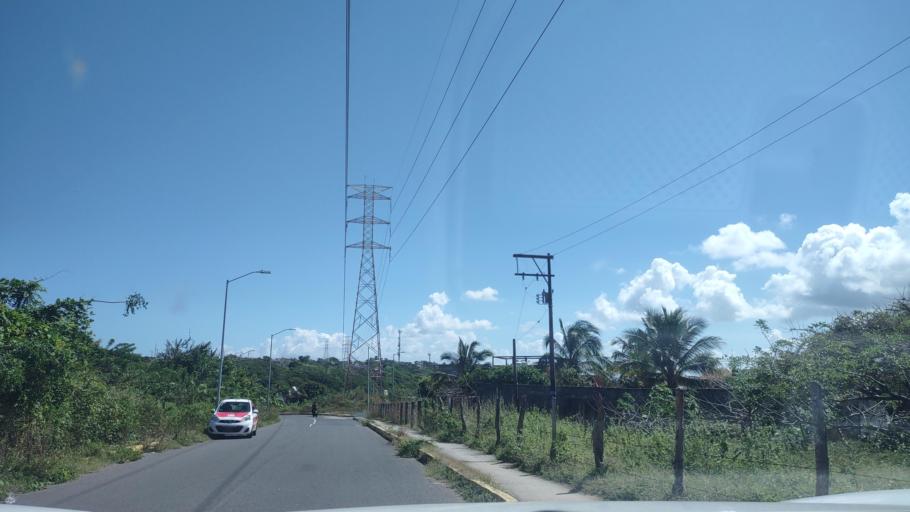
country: MX
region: Veracruz
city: Heroica Alvarado
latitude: 18.7785
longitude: -95.7642
